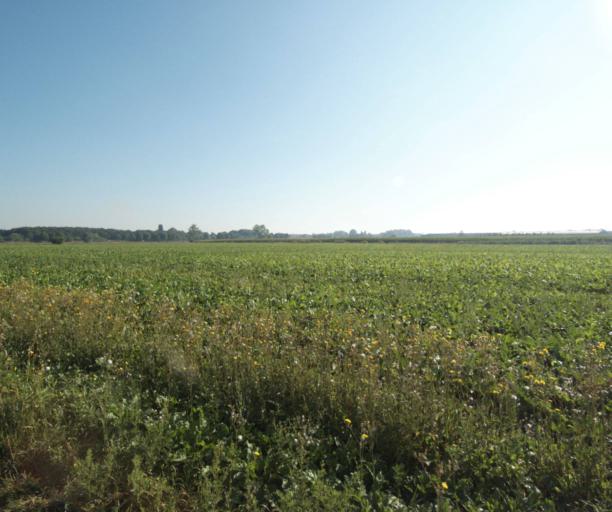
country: FR
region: Nord-Pas-de-Calais
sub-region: Departement du Nord
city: Wervicq-Sud
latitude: 50.7754
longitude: 3.0568
